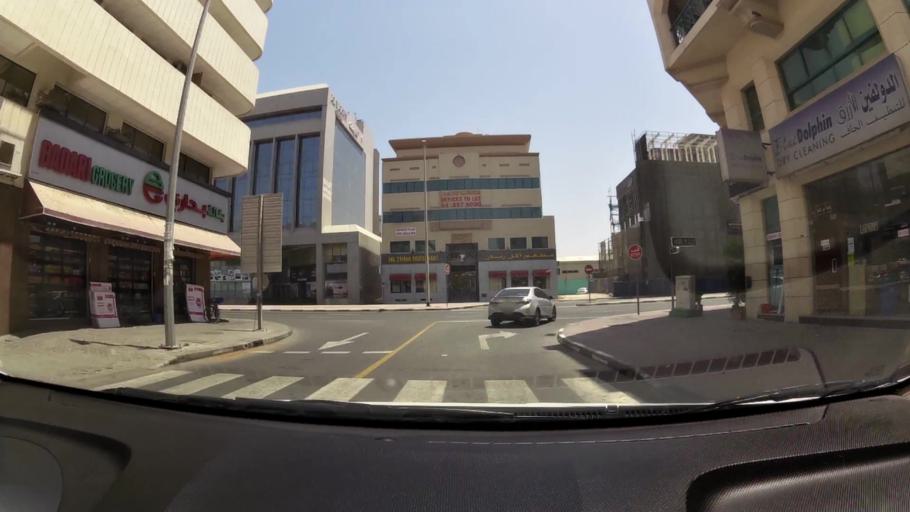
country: AE
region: Ash Shariqah
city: Sharjah
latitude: 25.2634
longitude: 55.3303
